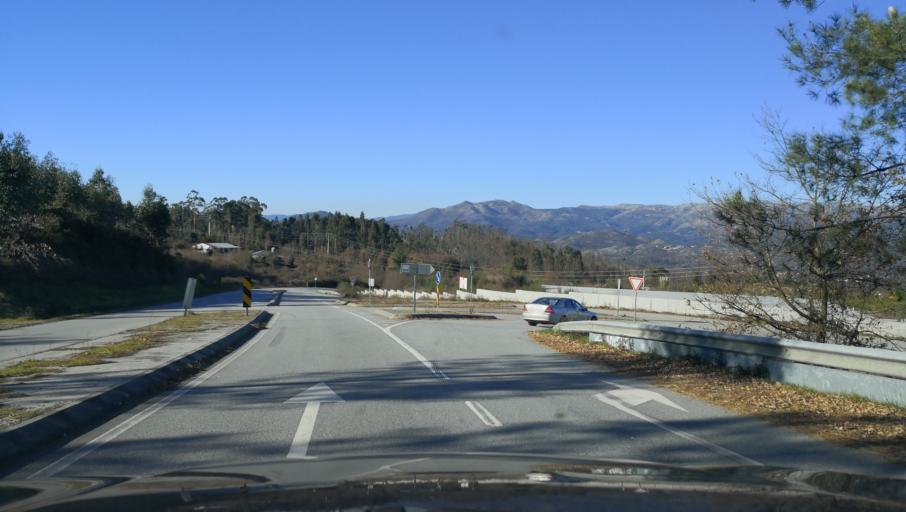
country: PT
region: Viseu
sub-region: Vouzela
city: Vouzela
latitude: 40.7211
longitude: -8.1313
